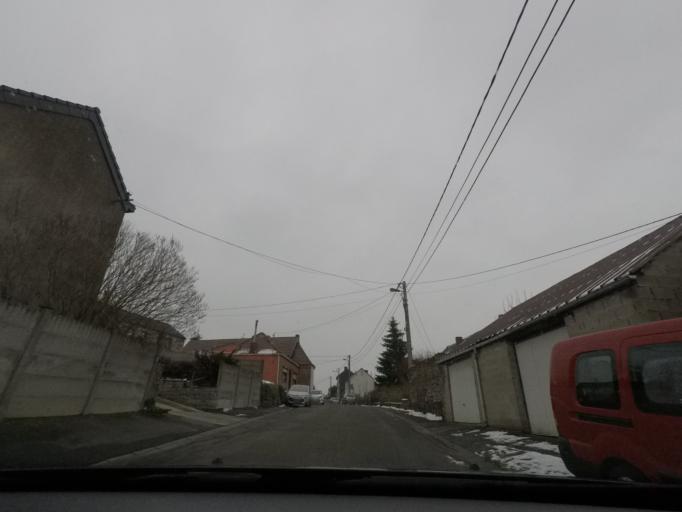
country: BE
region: Wallonia
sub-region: Province du Hainaut
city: Brugelette
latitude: 50.5937
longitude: 3.8731
